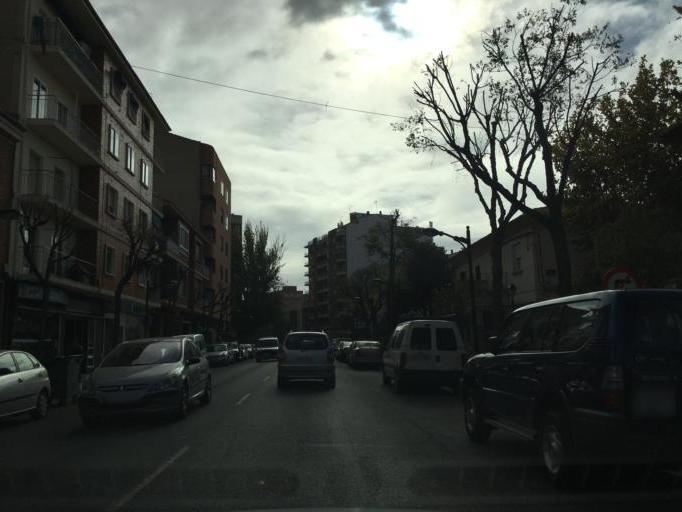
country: ES
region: Castille-La Mancha
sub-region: Provincia de Albacete
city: Albacete
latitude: 38.9922
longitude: -1.8667
